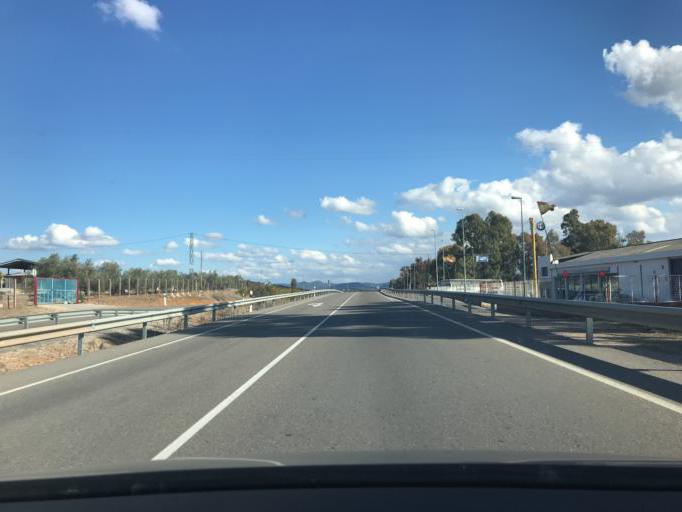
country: ES
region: Andalusia
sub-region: Province of Cordoba
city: Penarroya-Pueblonuevo
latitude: 38.2977
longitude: -5.2484
